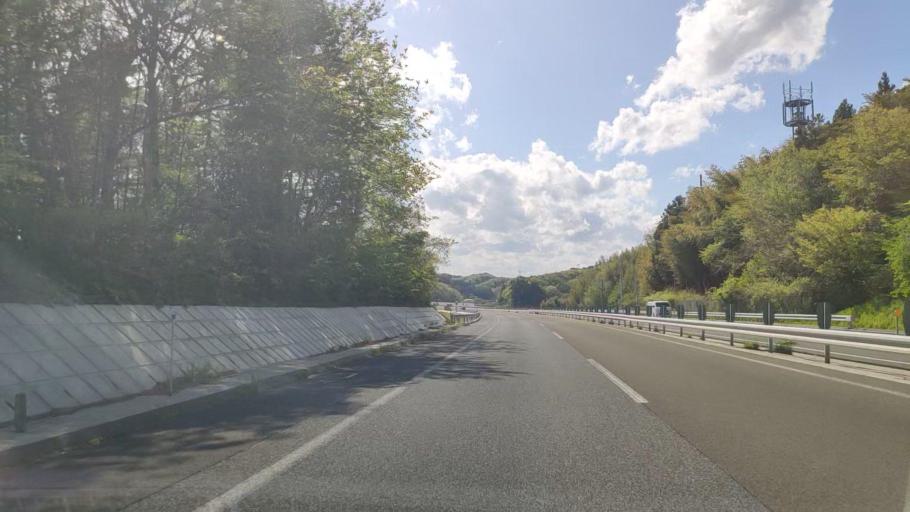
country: JP
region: Miyagi
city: Matsushima
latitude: 38.4129
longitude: 141.1025
